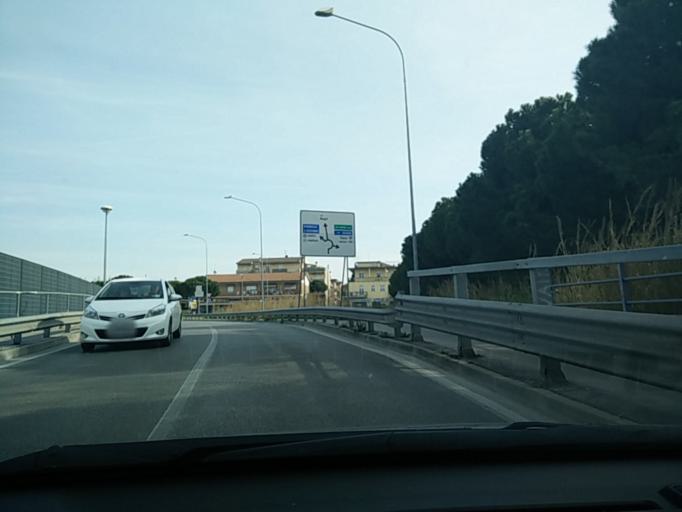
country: IT
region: Emilia-Romagna
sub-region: Provincia di Rimini
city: Rimini
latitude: 44.0698
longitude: 12.5412
